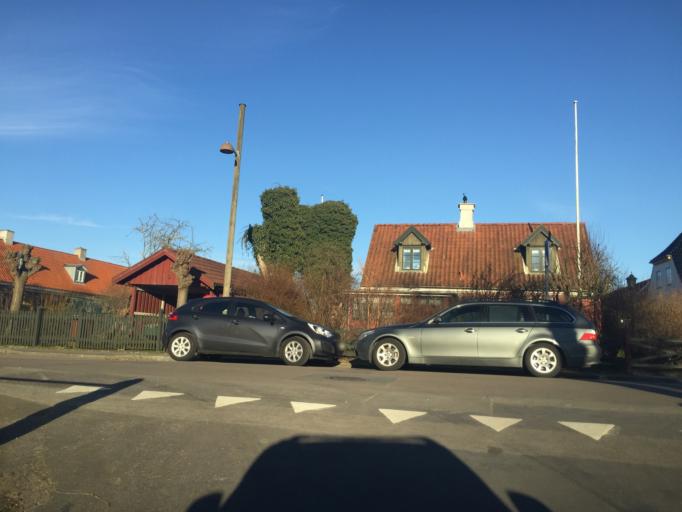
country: DK
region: Capital Region
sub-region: Dragor Kommune
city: Dragor
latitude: 55.5984
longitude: 12.6354
